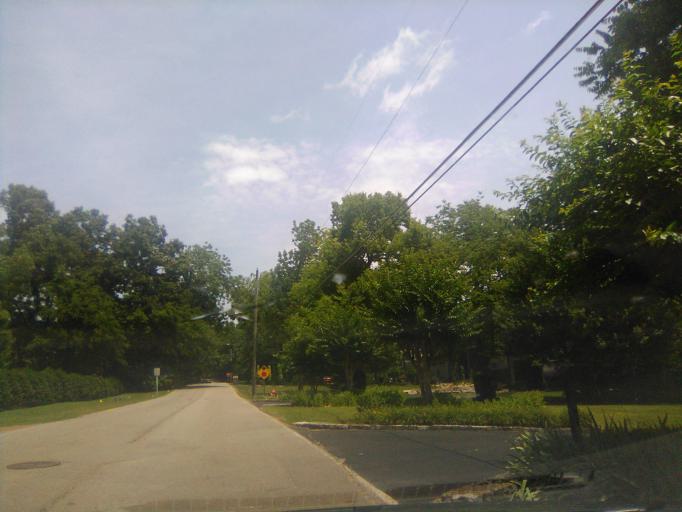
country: US
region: Tennessee
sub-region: Davidson County
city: Belle Meade
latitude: 36.0963
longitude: -86.8502
